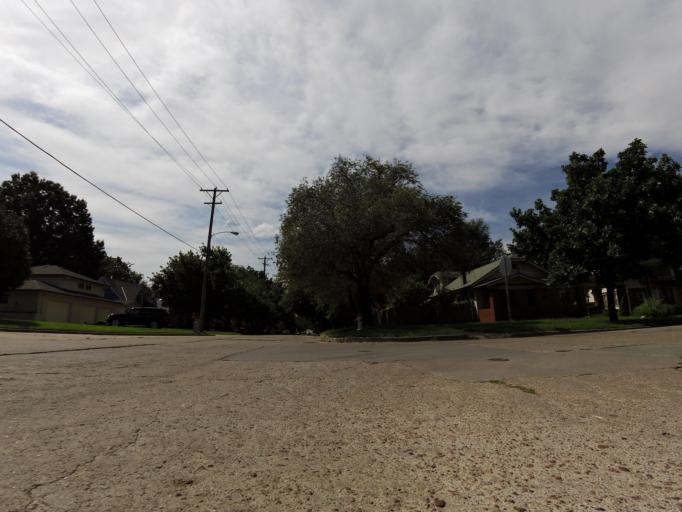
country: US
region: Kansas
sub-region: Sedgwick County
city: Wichita
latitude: 37.6975
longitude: -97.2936
